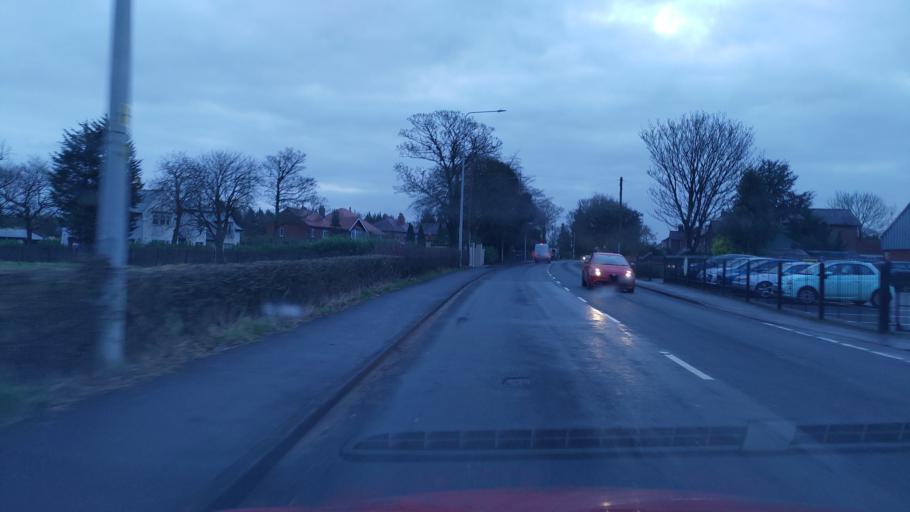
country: GB
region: England
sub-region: Lancashire
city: Coppull
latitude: 53.6281
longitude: -2.6824
